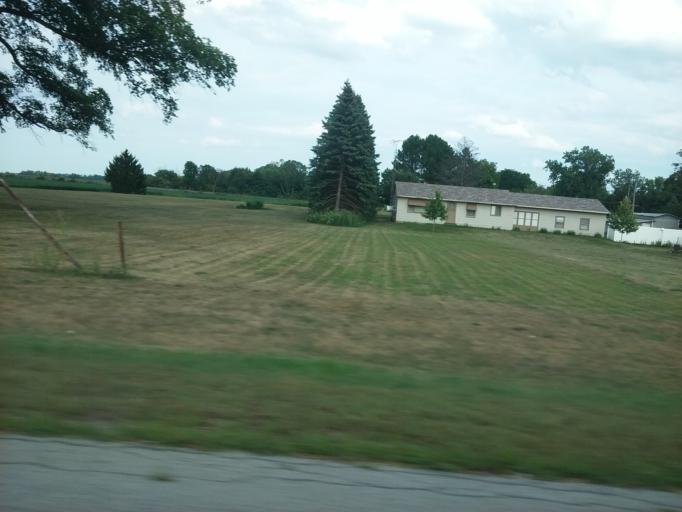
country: US
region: Ohio
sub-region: Wood County
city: Bowling Green
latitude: 41.3028
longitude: -83.6503
